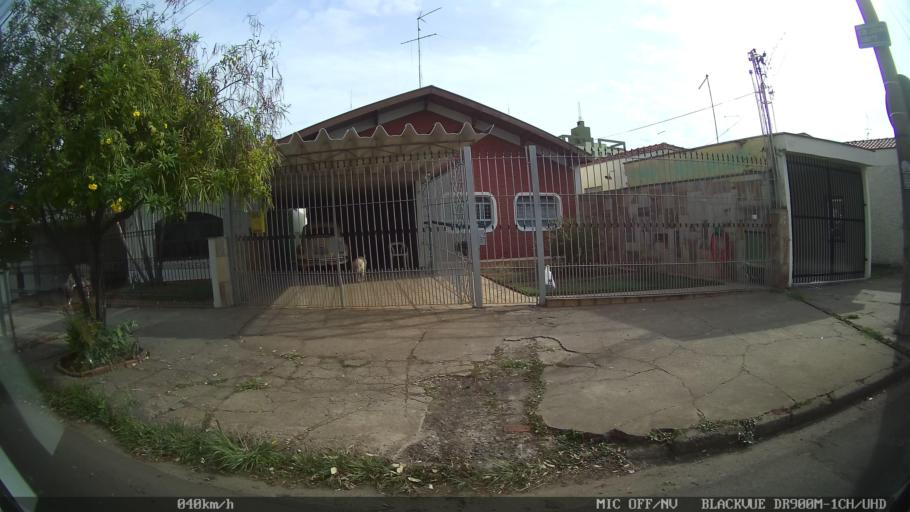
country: BR
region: Sao Paulo
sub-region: Piracicaba
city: Piracicaba
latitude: -22.7404
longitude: -47.6415
